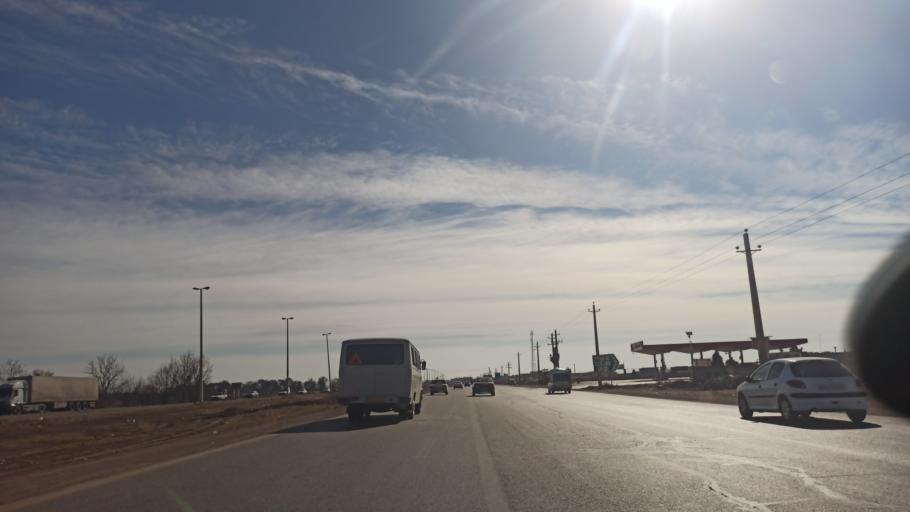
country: IR
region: Qazvin
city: Alvand
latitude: 36.1959
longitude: 50.0144
